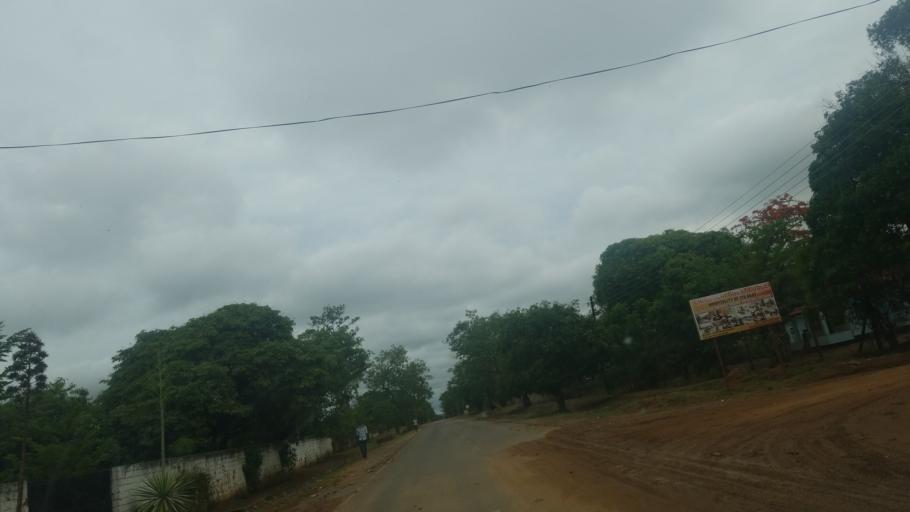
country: ZM
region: Luapula
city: Mansa
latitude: -11.1976
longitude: 28.8941
